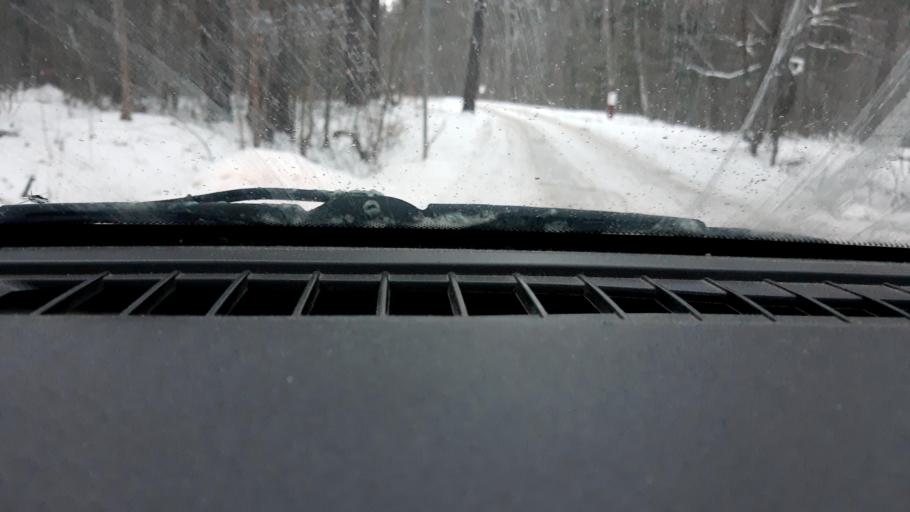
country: RU
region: Nizjnij Novgorod
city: Afonino
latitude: 56.1718
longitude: 44.0840
